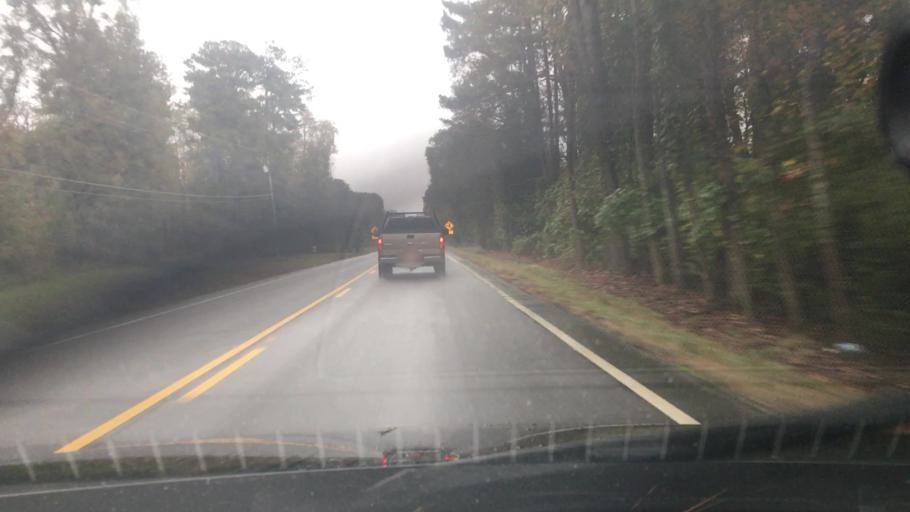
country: US
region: Georgia
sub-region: Spalding County
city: Experiment
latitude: 33.2410
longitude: -84.3919
